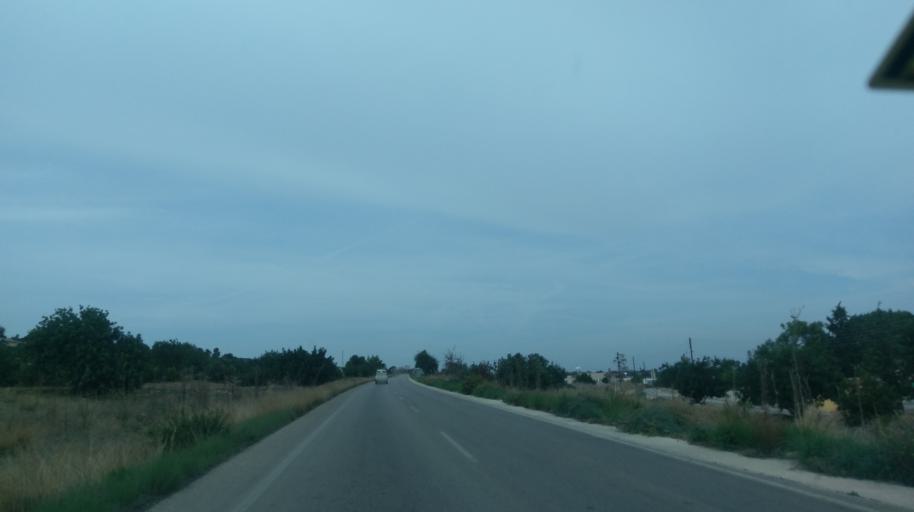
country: CY
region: Ammochostos
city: Leonarisso
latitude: 35.4239
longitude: 34.1262
